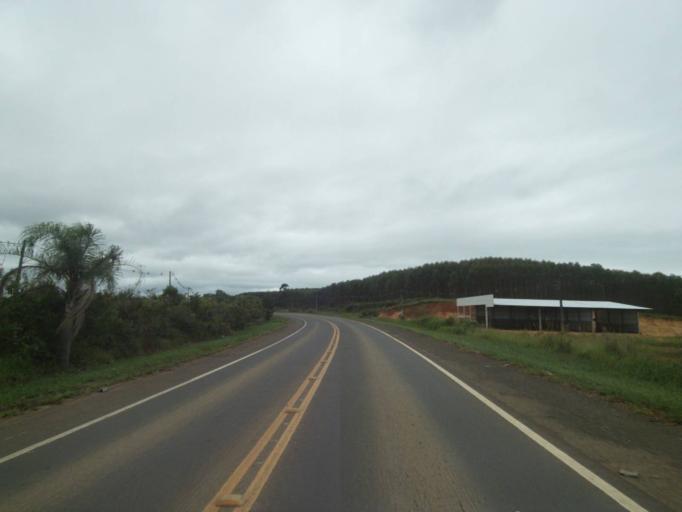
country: BR
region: Parana
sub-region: Telemaco Borba
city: Telemaco Borba
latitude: -24.3876
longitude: -50.6843
